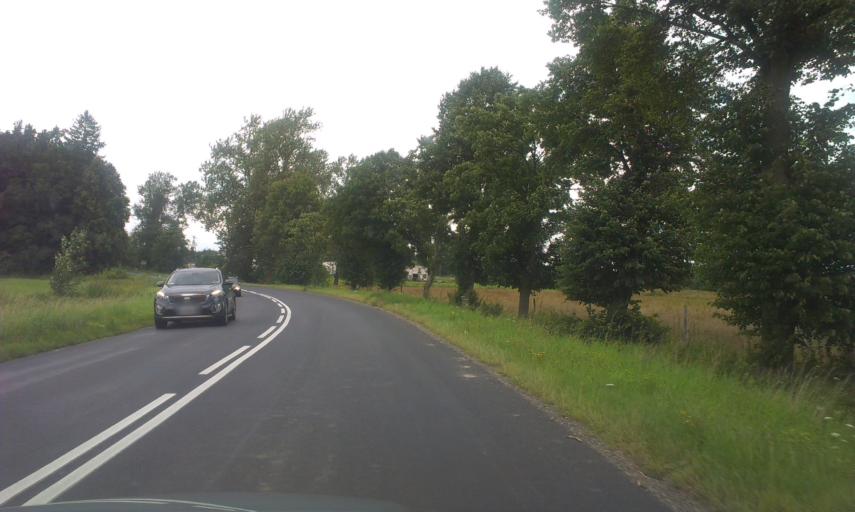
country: PL
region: West Pomeranian Voivodeship
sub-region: Powiat swidwinski
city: Rabino
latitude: 53.8881
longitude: 16.0694
